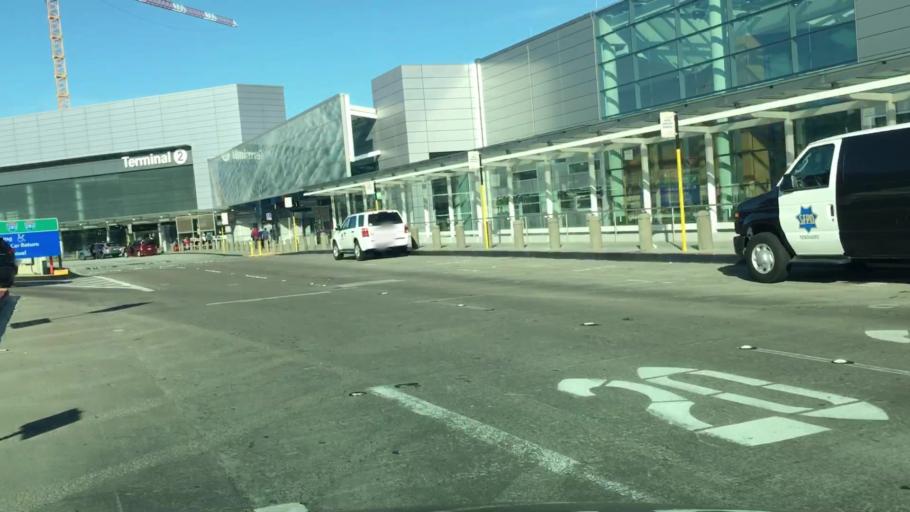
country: US
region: California
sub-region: San Mateo County
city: Millbrae
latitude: 37.6159
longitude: -122.3844
